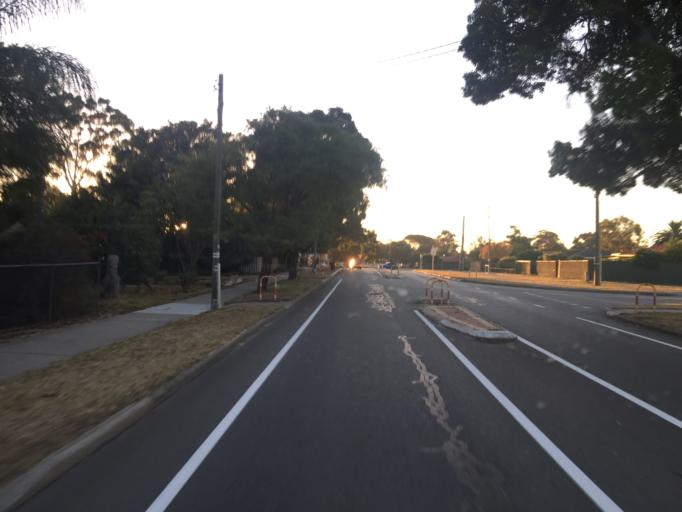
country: AU
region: Western Australia
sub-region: Gosnells
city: Maddington
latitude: -32.0330
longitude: 115.9837
